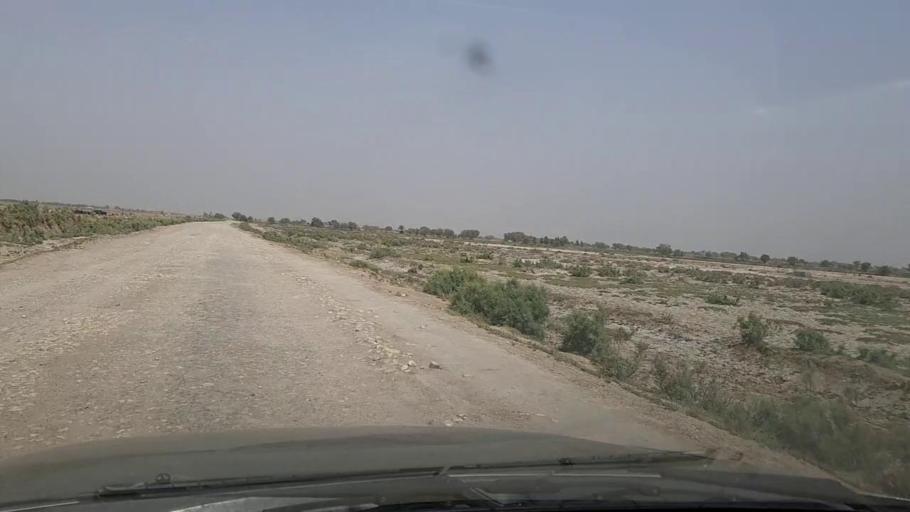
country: PK
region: Sindh
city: Thul
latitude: 28.4051
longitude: 68.7030
